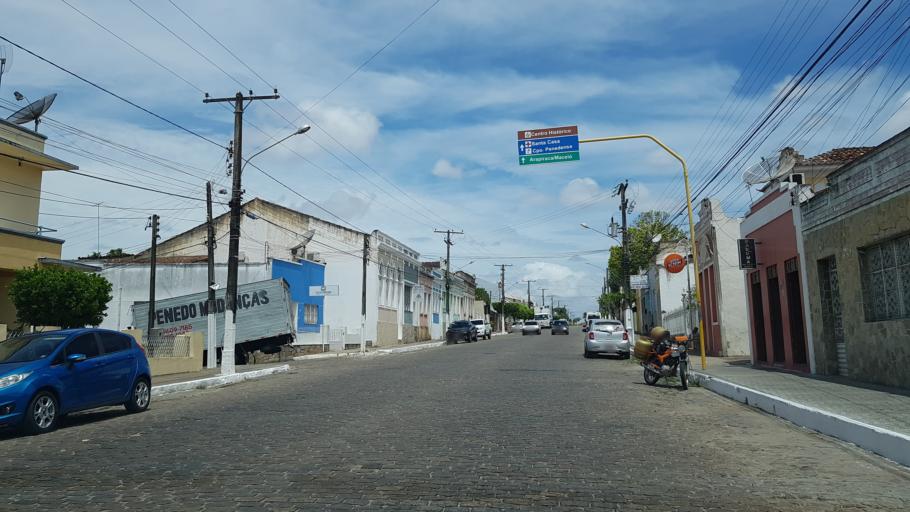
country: BR
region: Alagoas
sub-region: Penedo
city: Penedo
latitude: -10.2860
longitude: -36.5768
